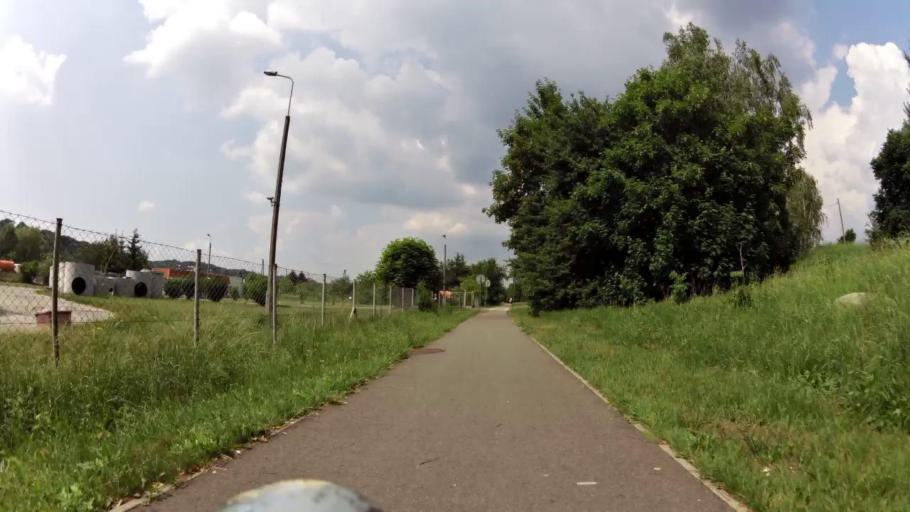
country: PL
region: Kujawsko-Pomorskie
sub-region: Powiat bydgoski
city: Koronowo
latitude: 53.3024
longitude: 17.9455
